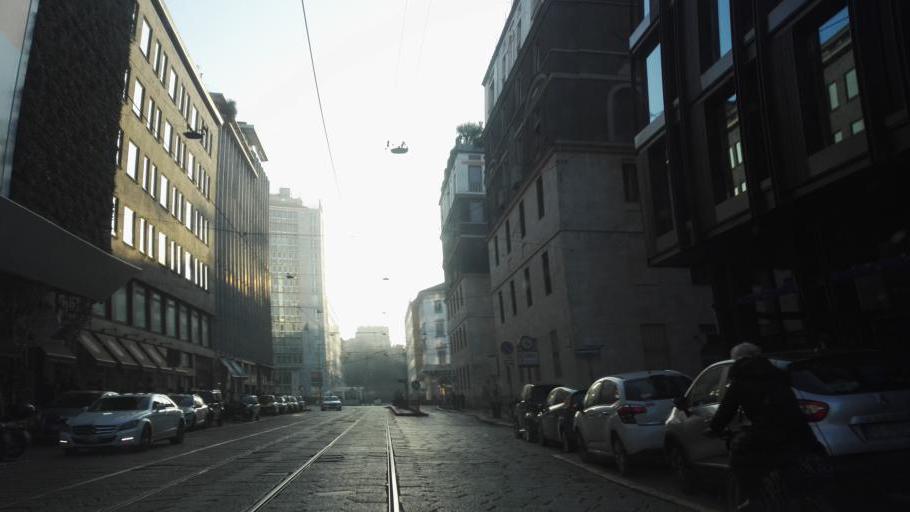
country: IT
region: Lombardy
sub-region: Citta metropolitana di Milano
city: Milano
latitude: 45.4766
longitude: 9.1953
